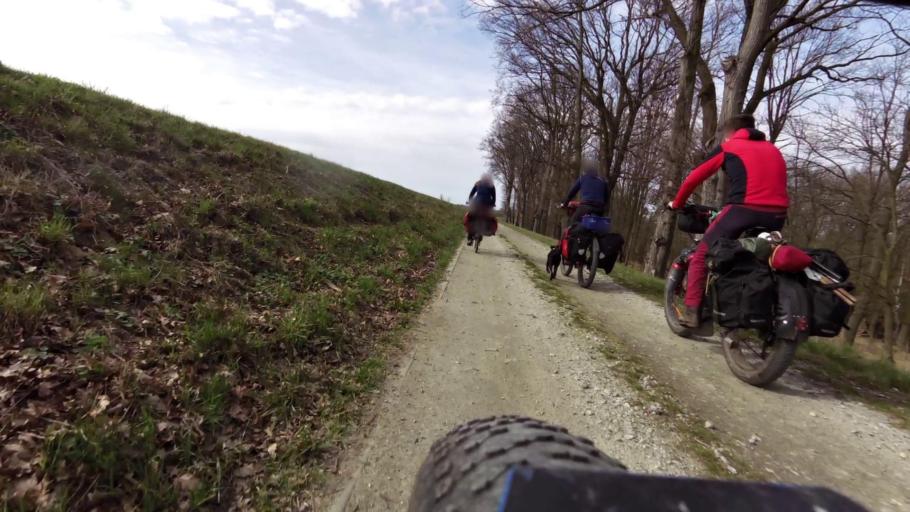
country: DE
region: Brandenburg
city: Reitwein
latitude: 52.5091
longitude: 14.6177
